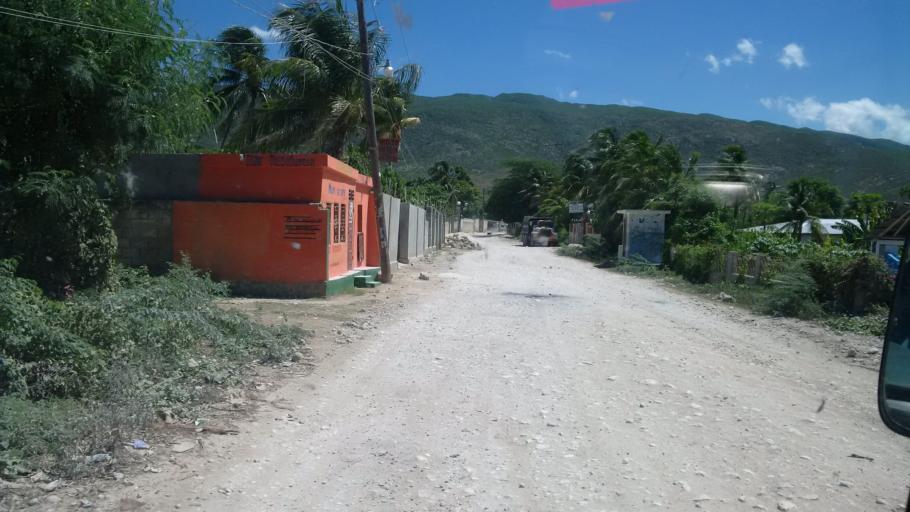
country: HT
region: Ouest
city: Thomazeau
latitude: 18.6558
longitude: -72.1515
